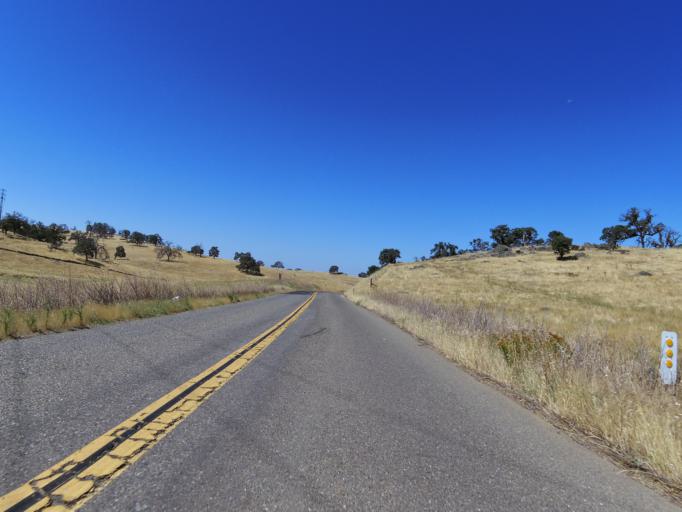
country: US
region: California
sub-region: Merced County
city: Planada
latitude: 37.5684
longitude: -120.3219
